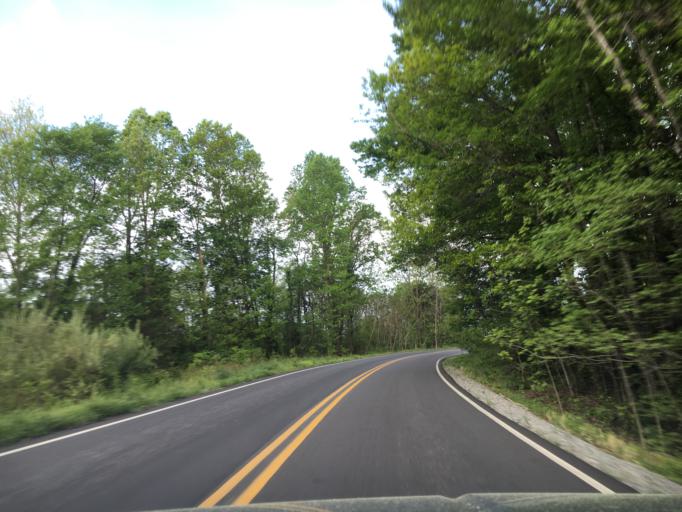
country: US
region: Virginia
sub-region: Halifax County
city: Halifax
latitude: 36.8907
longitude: -78.8372
